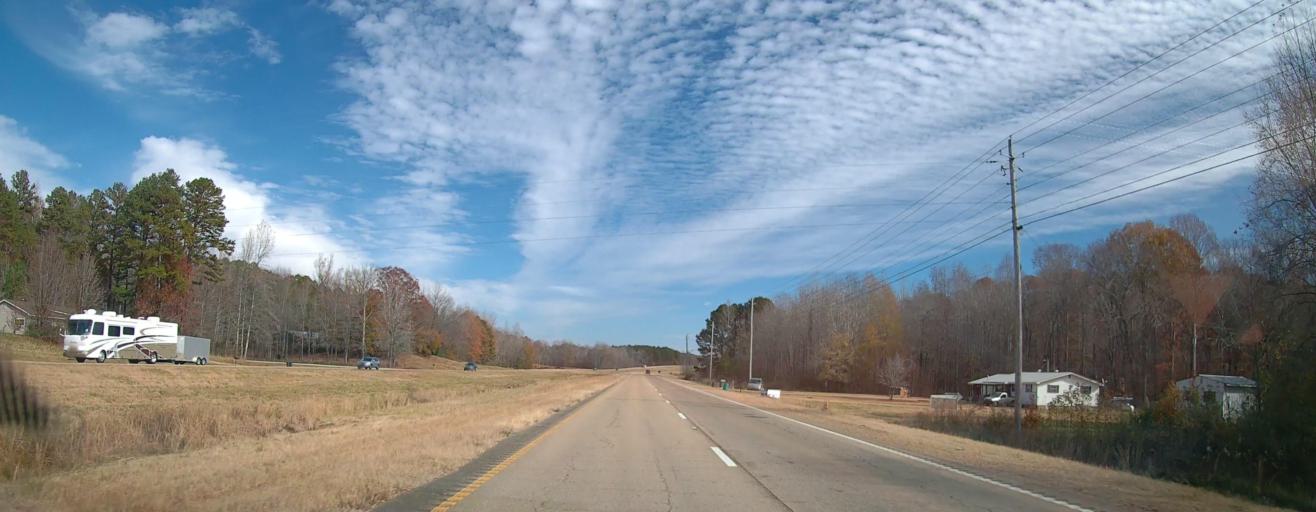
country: US
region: Mississippi
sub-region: Alcorn County
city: Corinth
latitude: 34.9351
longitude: -88.7436
